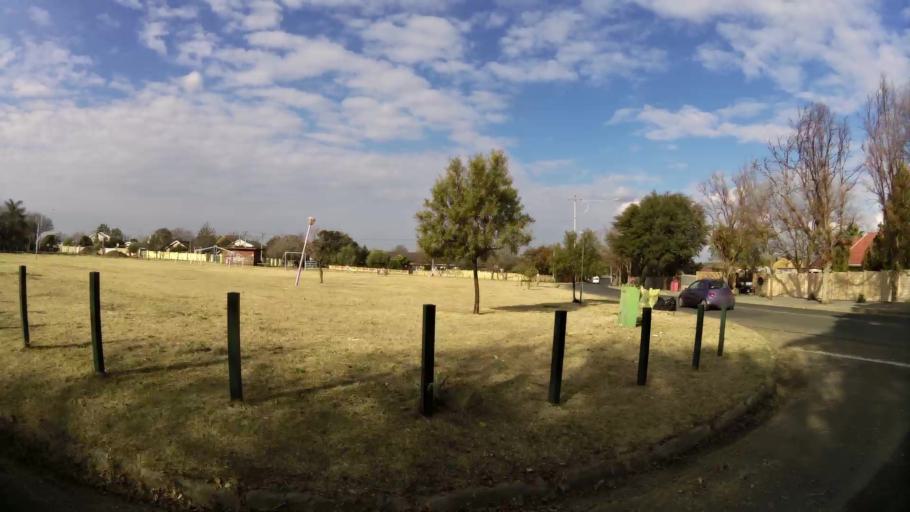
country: ZA
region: Orange Free State
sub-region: Mangaung Metropolitan Municipality
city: Bloemfontein
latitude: -29.0790
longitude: 26.2107
